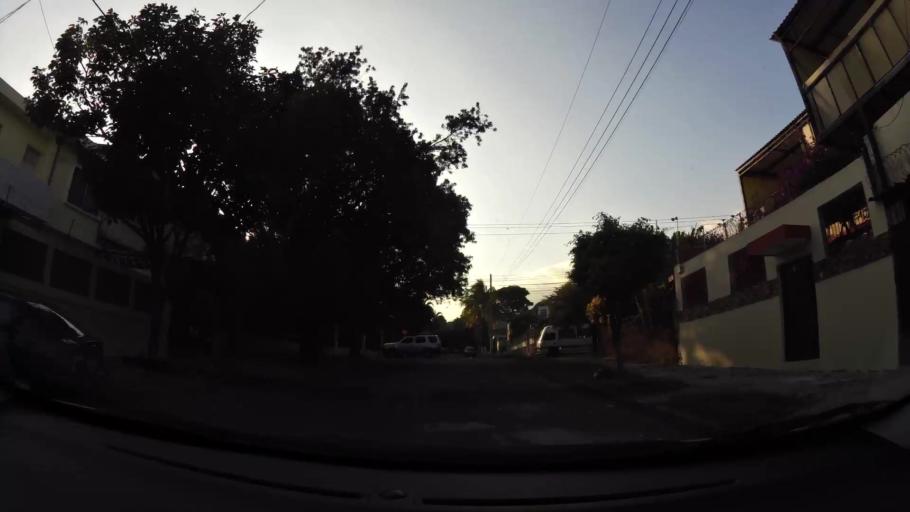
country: SV
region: San Salvador
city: Mejicanos
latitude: 13.7152
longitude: -89.2004
